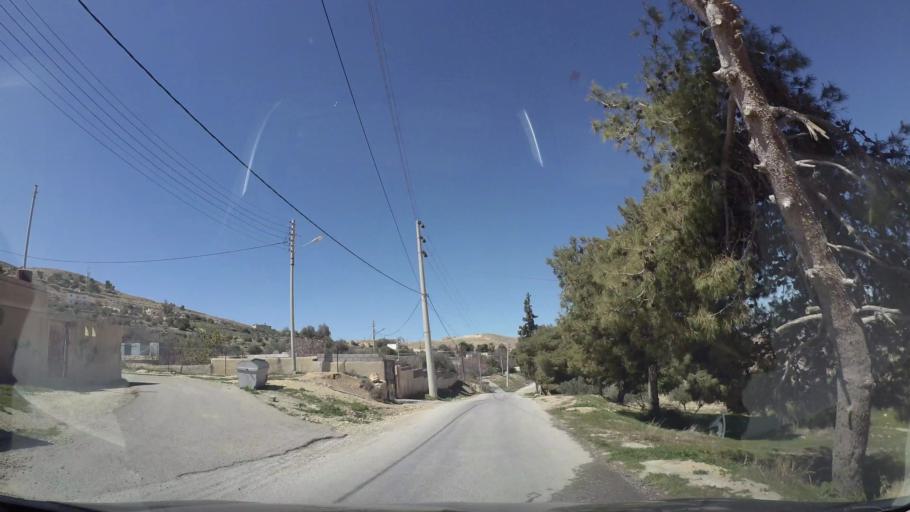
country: JO
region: Tafielah
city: At Tafilah
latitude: 30.8397
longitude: 35.5705
